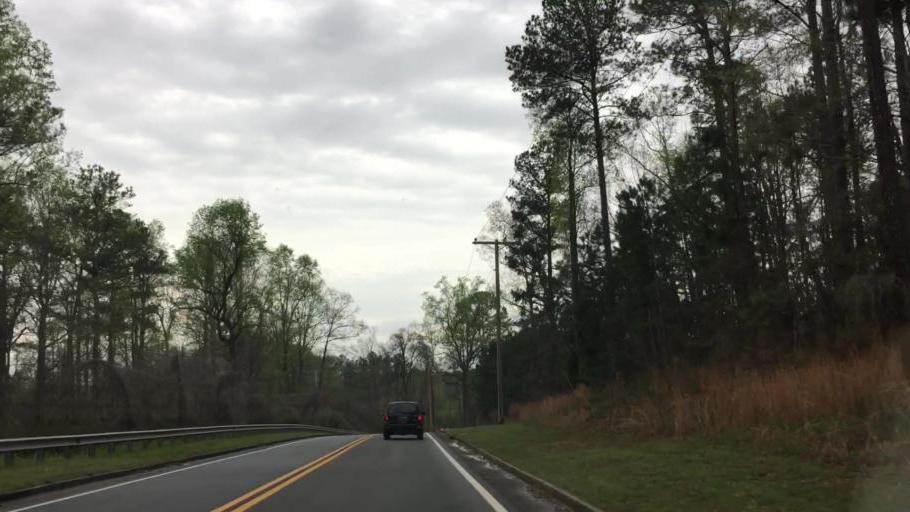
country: US
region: Georgia
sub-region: Fulton County
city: Milton
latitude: 34.1898
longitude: -84.3055
